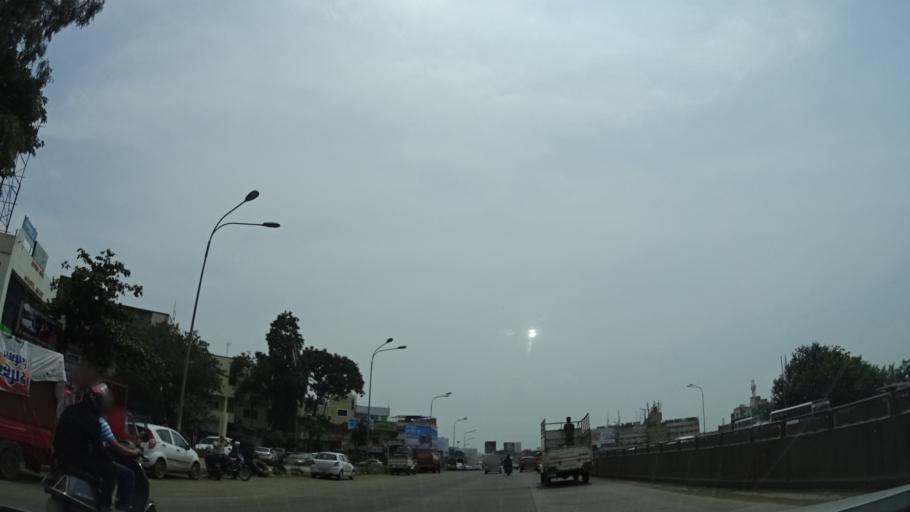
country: IN
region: Maharashtra
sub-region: Pune Division
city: Lohogaon
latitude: 18.5631
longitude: 73.9363
